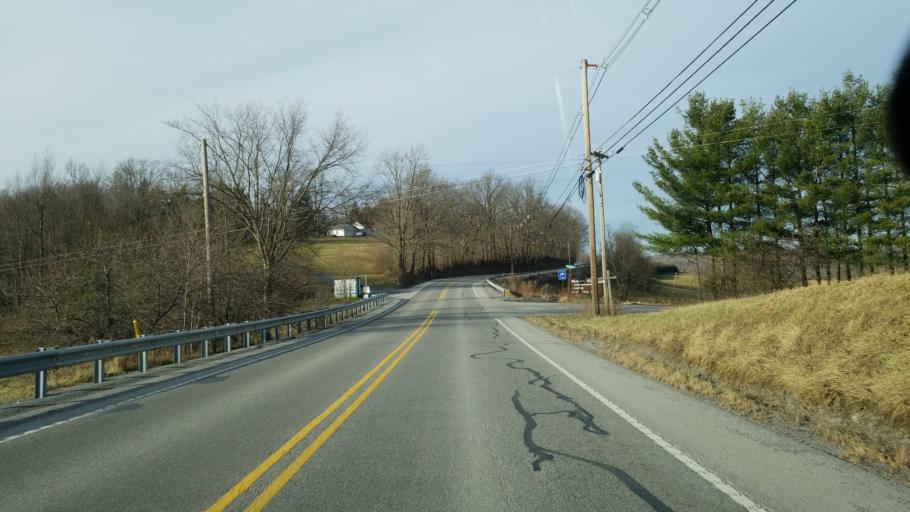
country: US
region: Pennsylvania
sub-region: Clearfield County
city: Curwensville
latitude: 40.9927
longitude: -78.6288
